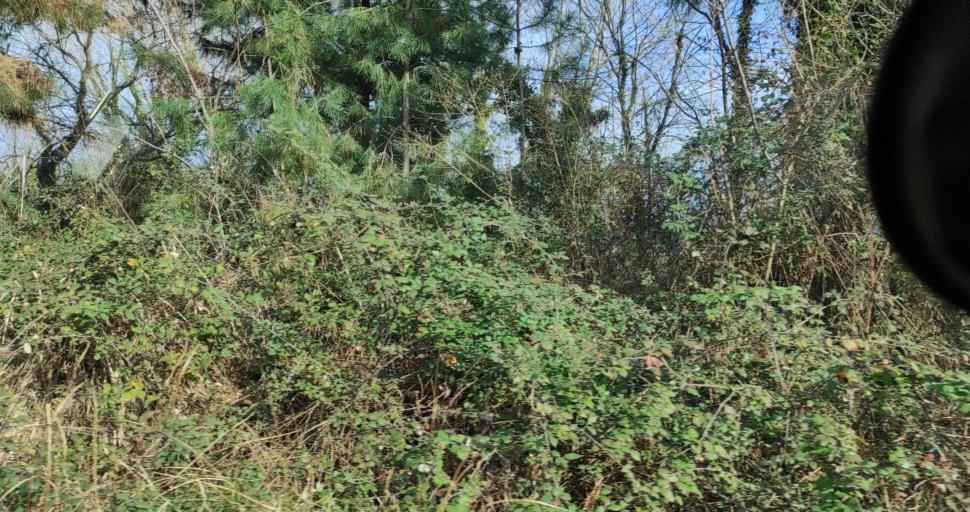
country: AL
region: Lezhe
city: Shengjin
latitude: 41.7794
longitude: 19.6034
